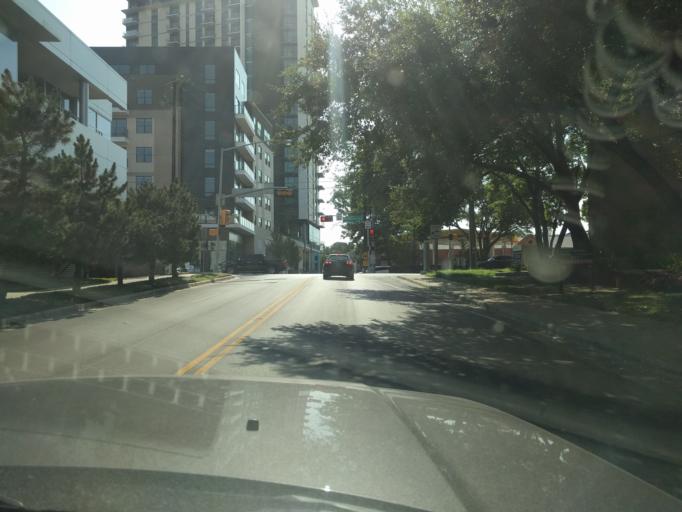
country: US
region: Texas
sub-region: Dallas County
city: Dallas
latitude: 32.8032
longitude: -96.8007
